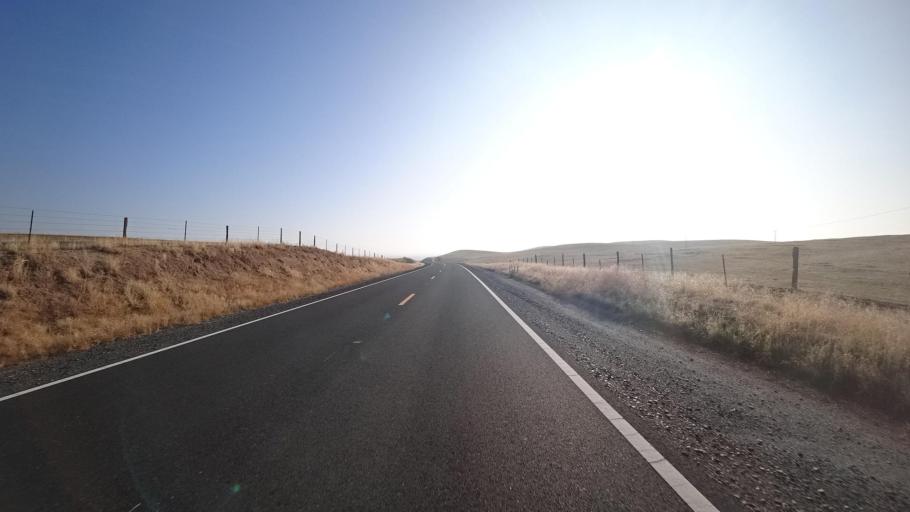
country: US
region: California
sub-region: Tulare County
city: Richgrove
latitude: 35.7499
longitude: -118.9940
